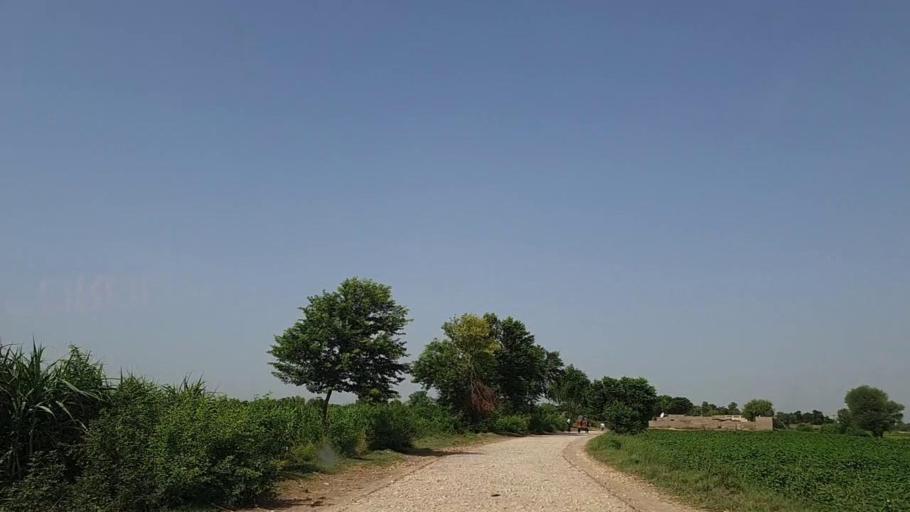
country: PK
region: Sindh
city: Naushahro Firoz
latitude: 26.8741
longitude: 68.0384
